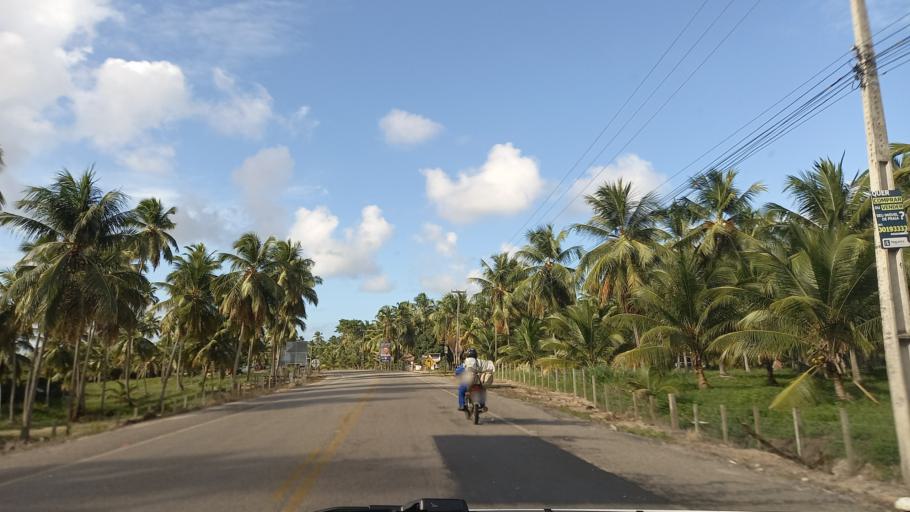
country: BR
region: Pernambuco
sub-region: Tamandare
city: Tamandare
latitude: -8.7081
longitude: -35.0880
